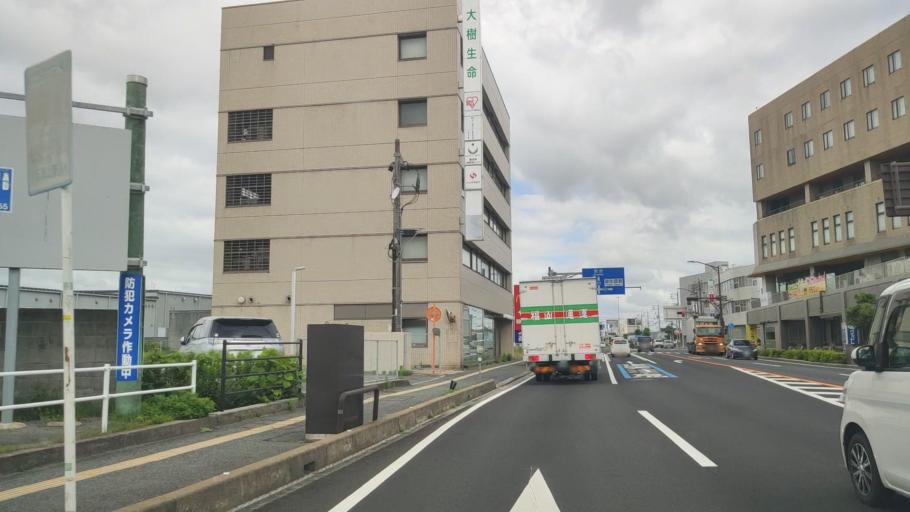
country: JP
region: Tottori
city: Yonago
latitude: 35.4384
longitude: 133.3421
